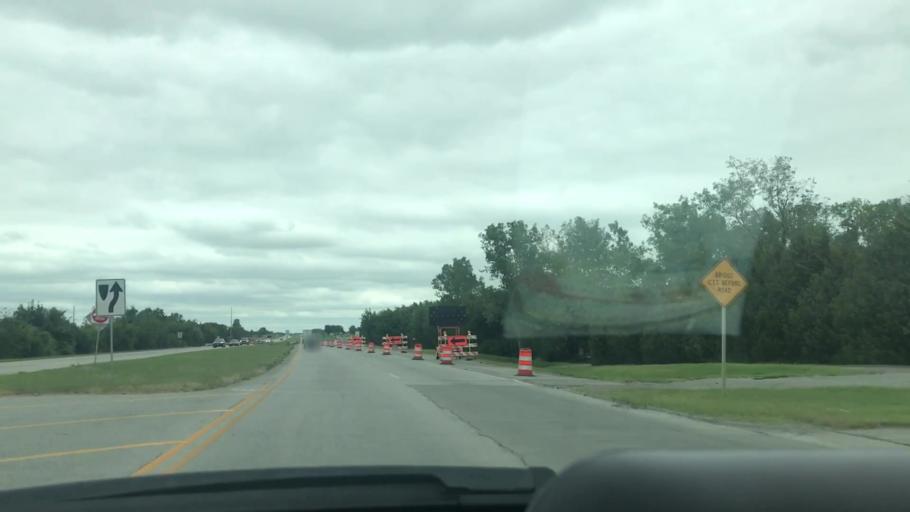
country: US
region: Oklahoma
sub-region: Mayes County
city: Pryor
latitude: 36.3181
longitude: -95.3149
